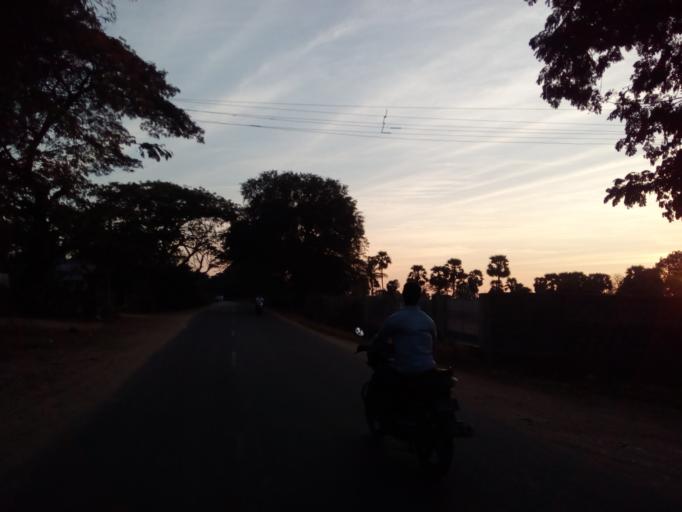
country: IN
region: Andhra Pradesh
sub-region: Prakasam
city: Vetapalem
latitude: 15.7238
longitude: 80.2540
